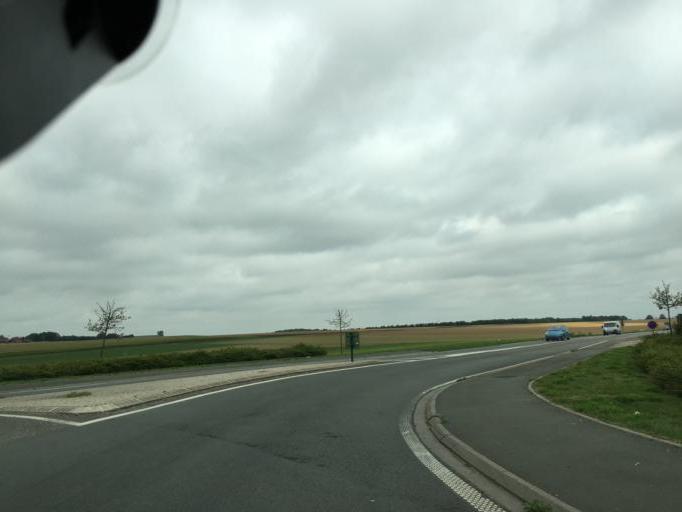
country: FR
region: Nord-Pas-de-Calais
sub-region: Departement du Pas-de-Calais
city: Saint-Pol-sur-Ternoise
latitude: 50.3911
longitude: 2.3529
